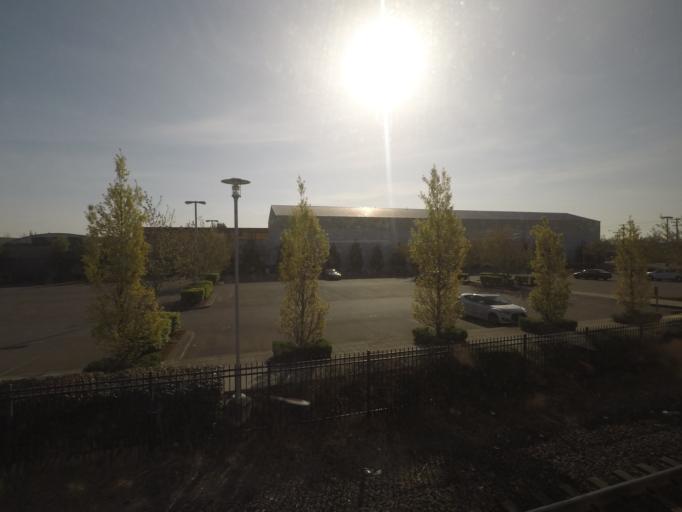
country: US
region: Washington
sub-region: Snohomish County
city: Everett
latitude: 47.9749
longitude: -122.1970
